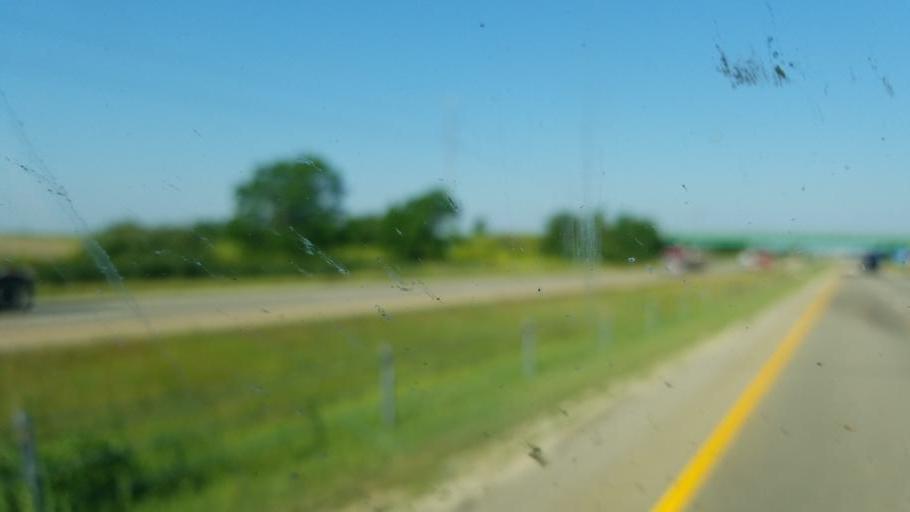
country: US
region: Illinois
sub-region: LaSalle County
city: Deer Park
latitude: 41.3680
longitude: -88.9700
